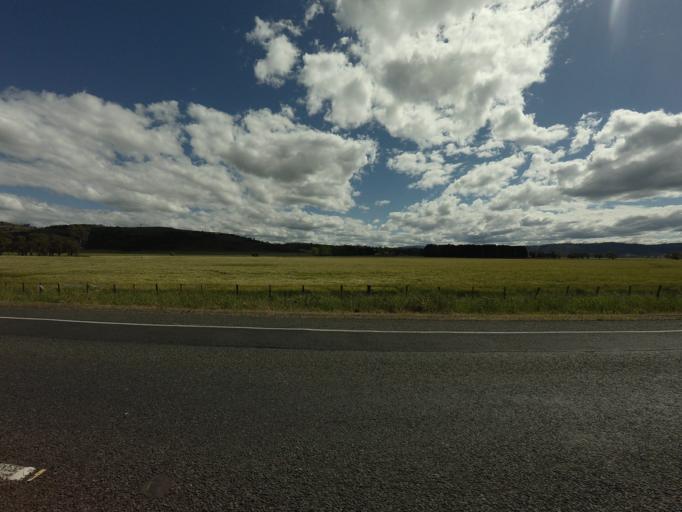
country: AU
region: Tasmania
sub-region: Northern Midlands
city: Evandale
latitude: -42.0310
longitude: 147.4790
